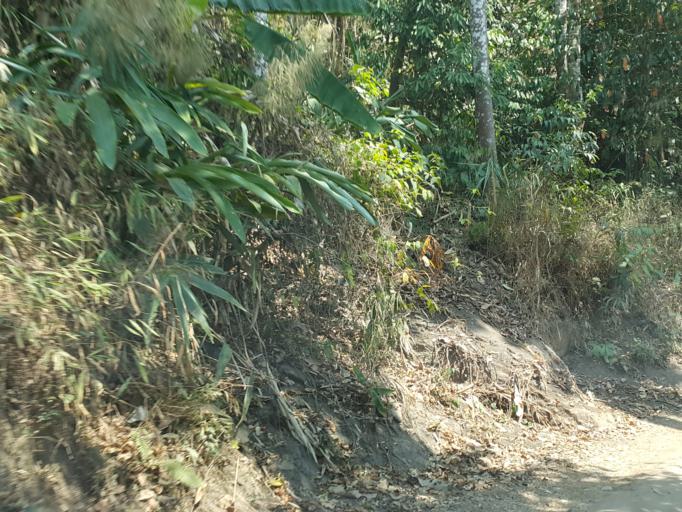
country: TH
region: Chiang Mai
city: Samoeng
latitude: 18.8861
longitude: 98.7831
